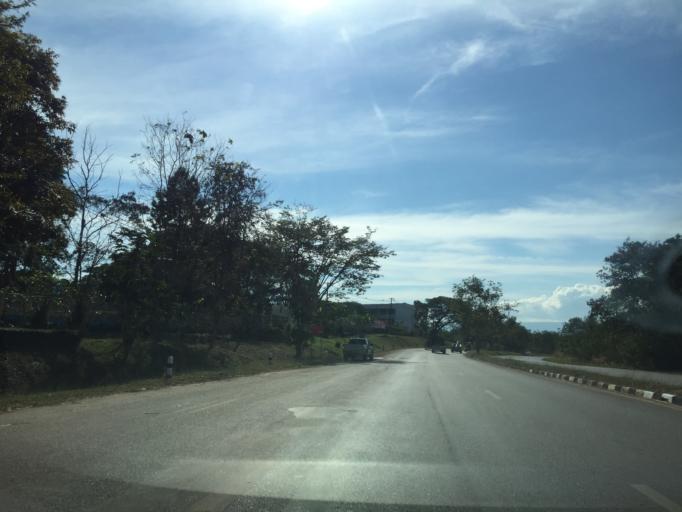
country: TH
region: Loei
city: Wang Saphung
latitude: 17.3037
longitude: 101.8014
